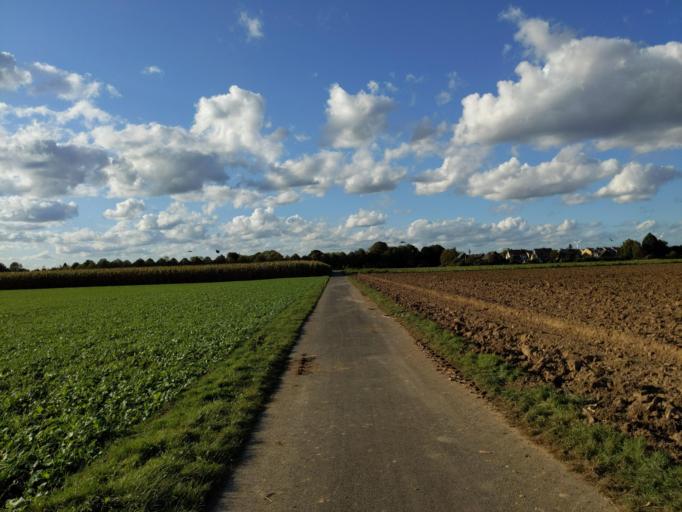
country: DE
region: North Rhine-Westphalia
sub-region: Regierungsbezirk Dusseldorf
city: Kaarst
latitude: 51.2112
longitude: 6.5912
